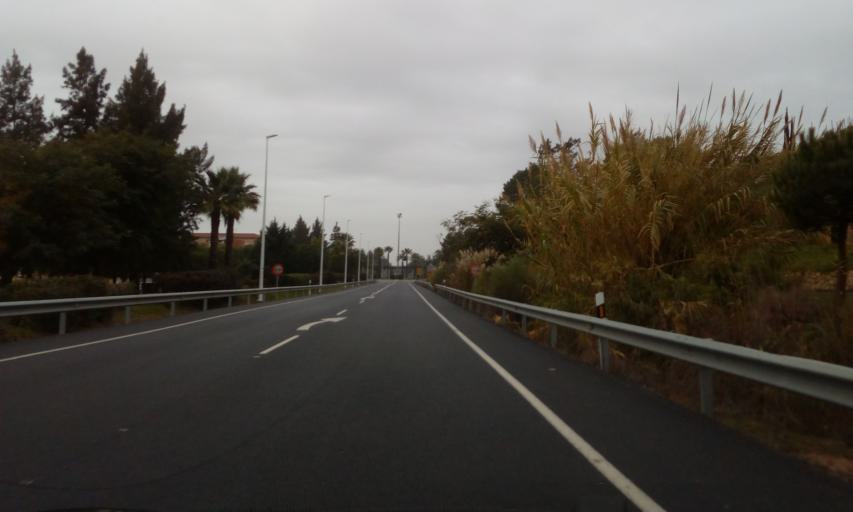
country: ES
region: Andalusia
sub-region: Provincia de Huelva
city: Lepe
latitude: 37.2091
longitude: -7.2268
